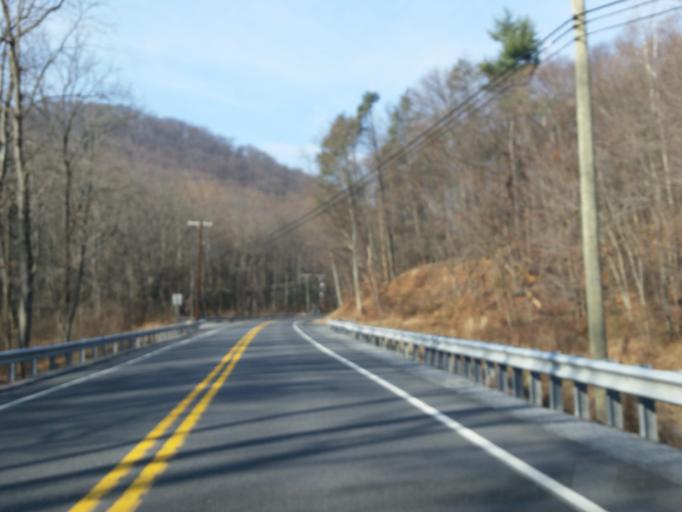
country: US
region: Pennsylvania
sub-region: Lebanon County
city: Jonestown
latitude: 40.4381
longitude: -76.5970
